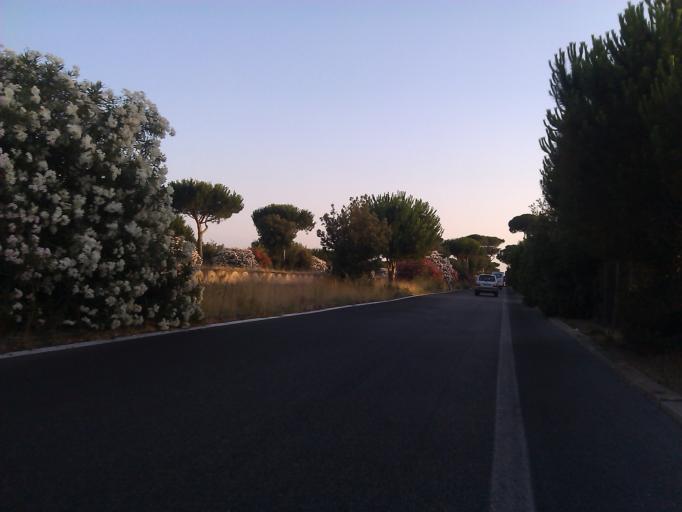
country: IT
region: Latium
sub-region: Citta metropolitana di Roma Capitale
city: Acilia-Castel Fusano-Ostia Antica
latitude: 41.7277
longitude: 12.3341
